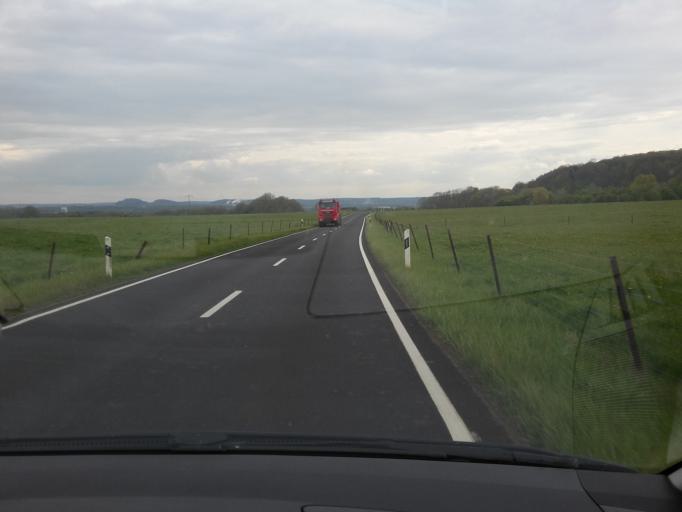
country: LU
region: Luxembourg
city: Hautcharage
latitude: 49.5941
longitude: 5.9135
